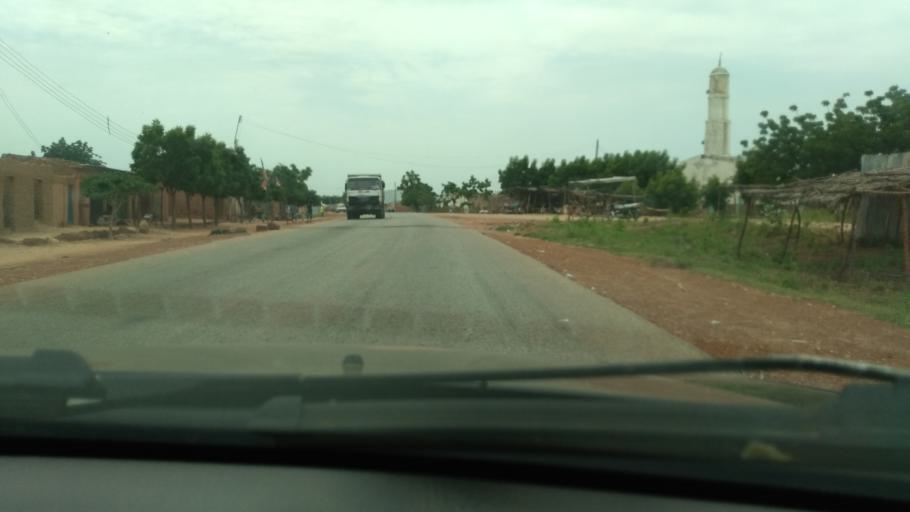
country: NG
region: Katsina
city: Kankia
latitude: 12.4060
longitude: 7.7205
